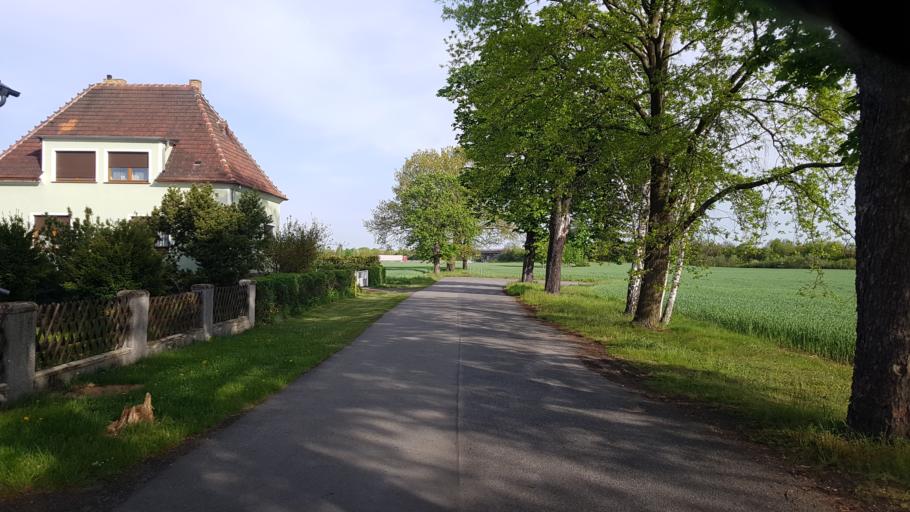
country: DE
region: Brandenburg
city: Ortrand
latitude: 51.3818
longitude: 13.7530
